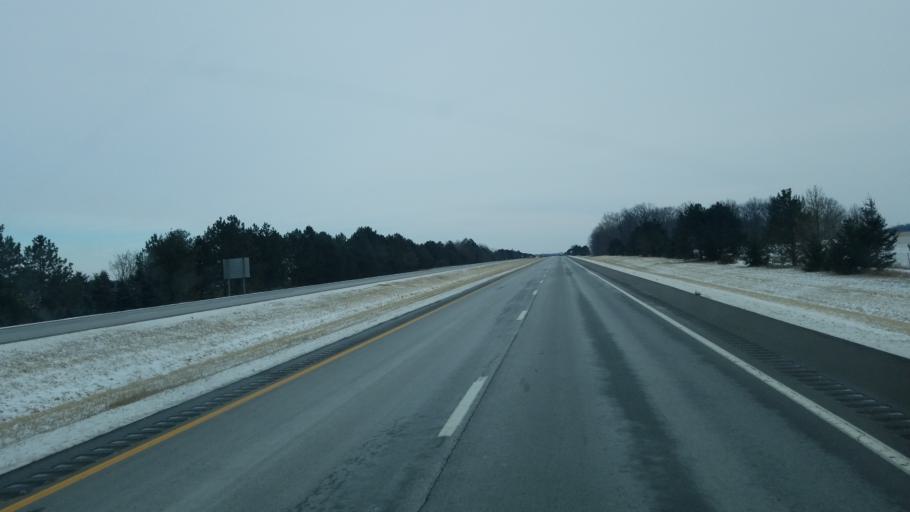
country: US
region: Ohio
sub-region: Wyandot County
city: Carey
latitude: 40.9622
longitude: -83.4661
